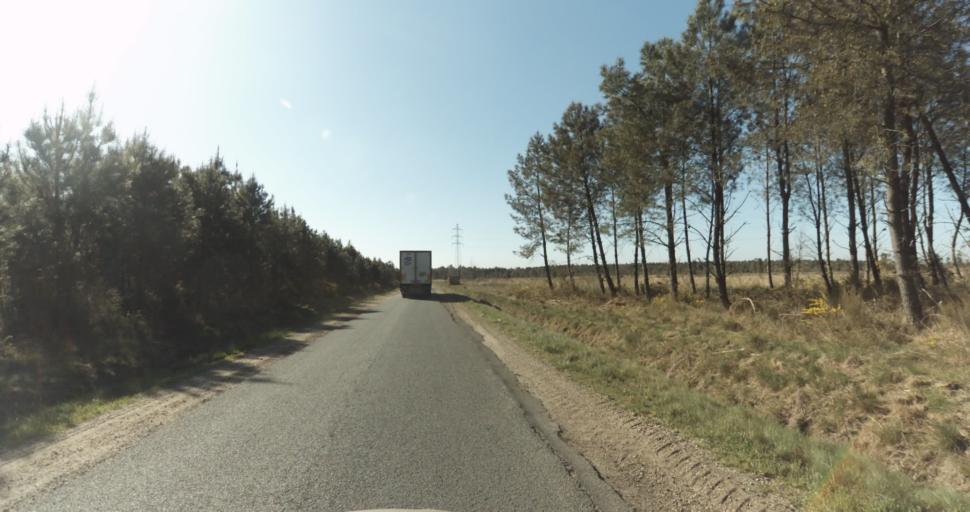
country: FR
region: Aquitaine
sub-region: Departement de la Gironde
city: Marcheprime
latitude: 44.7528
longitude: -0.8489
